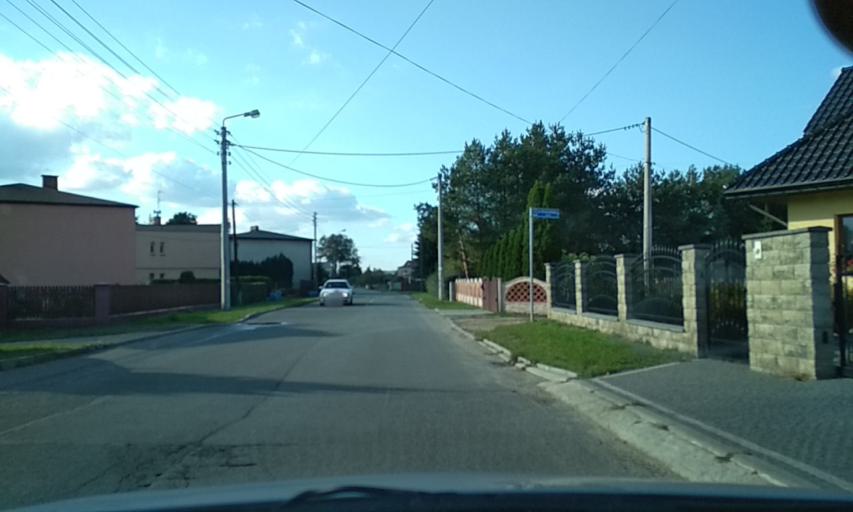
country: PL
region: Silesian Voivodeship
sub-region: Powiat bierunsko-ledzinski
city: Ledziny
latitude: 50.1726
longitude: 19.1443
